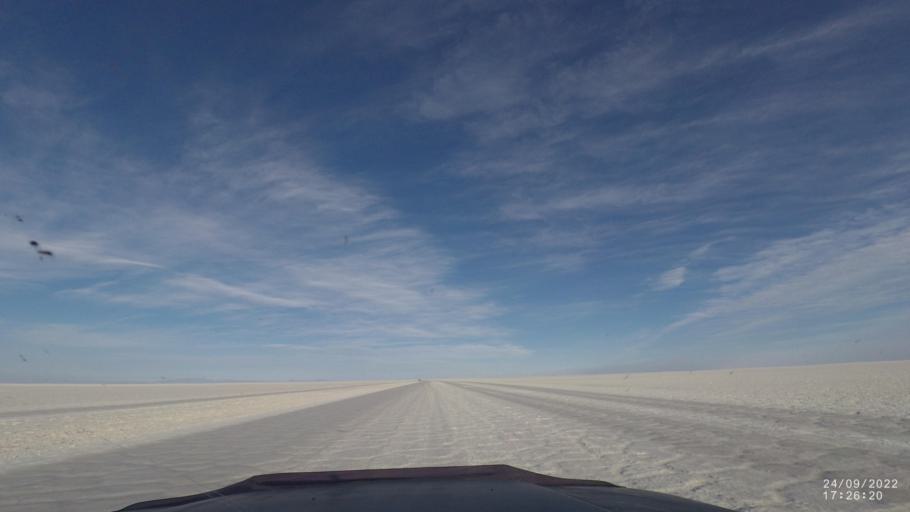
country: BO
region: Potosi
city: Colchani
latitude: -20.2943
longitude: -67.4706
